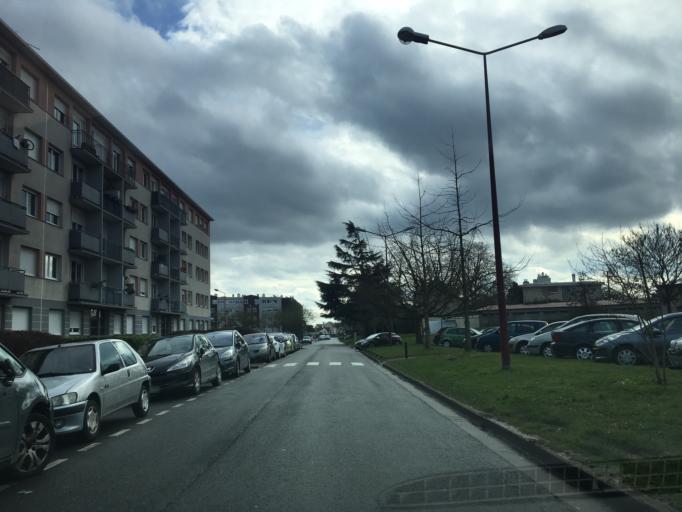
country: FR
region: Ile-de-France
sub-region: Departement du Val-d'Oise
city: Arnouville
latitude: 49.0023
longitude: 2.4194
